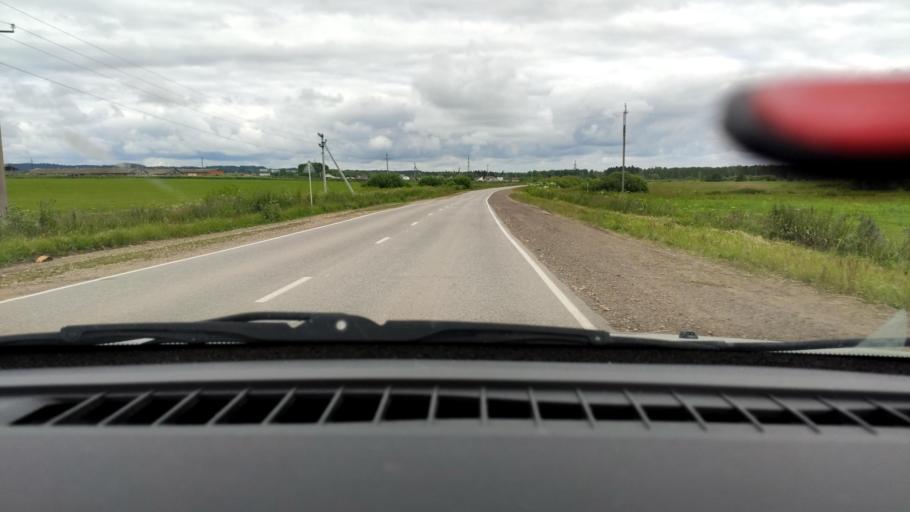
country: RU
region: Perm
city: Ust'-Kachka
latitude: 58.0747
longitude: 55.6213
